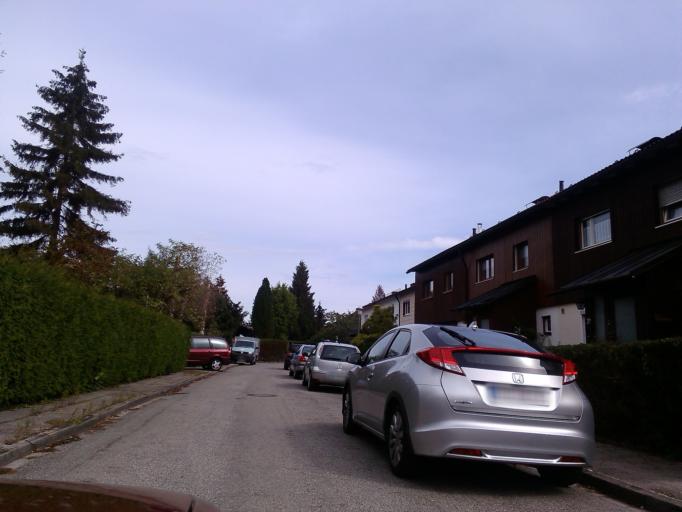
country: DE
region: Bavaria
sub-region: Upper Bavaria
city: Starnberg
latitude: 48.0091
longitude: 11.3209
